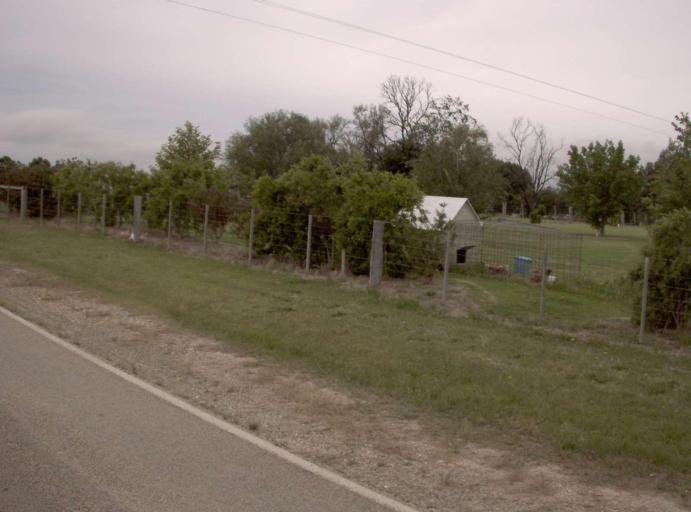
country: AU
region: Victoria
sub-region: East Gippsland
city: Bairnsdale
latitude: -37.8171
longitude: 147.4362
